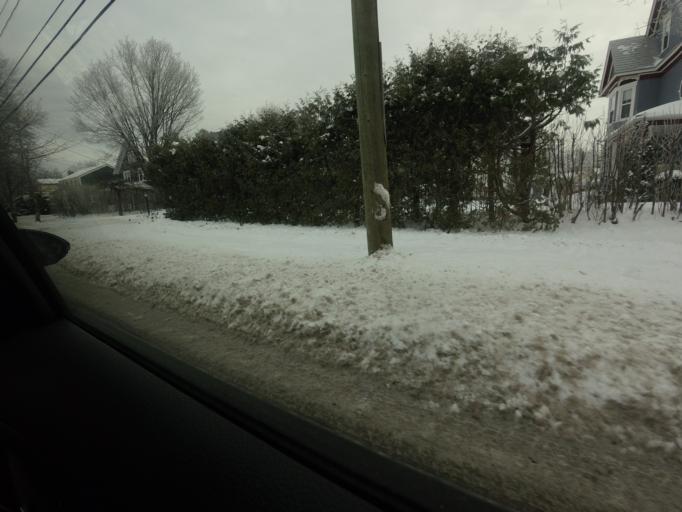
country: CA
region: New Brunswick
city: Fredericton
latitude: 45.9525
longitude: -66.6366
